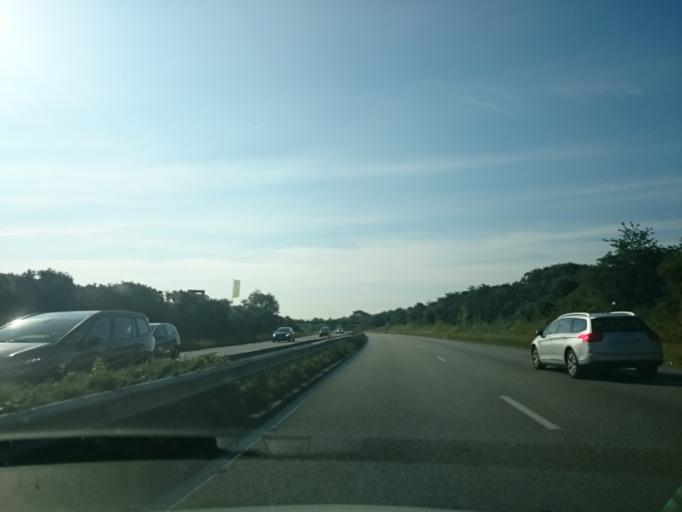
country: FR
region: Brittany
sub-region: Departement du Finistere
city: Ergue-Gaberic
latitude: 47.9738
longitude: -4.0069
